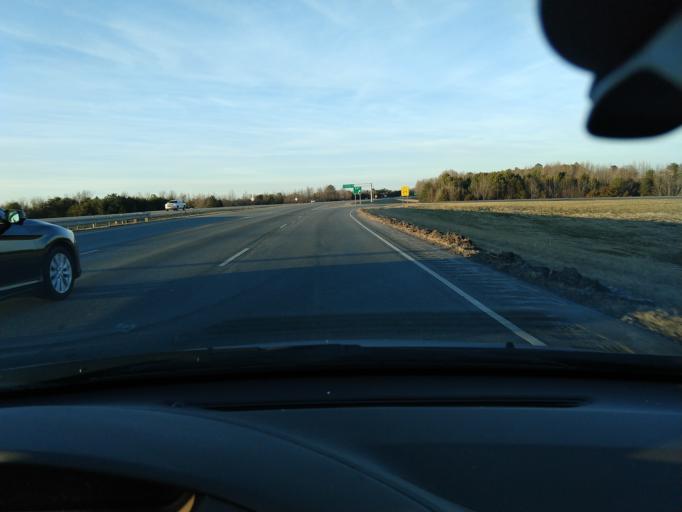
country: US
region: North Carolina
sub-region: Guilford County
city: Oak Ridge
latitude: 36.0946
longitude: -79.9663
